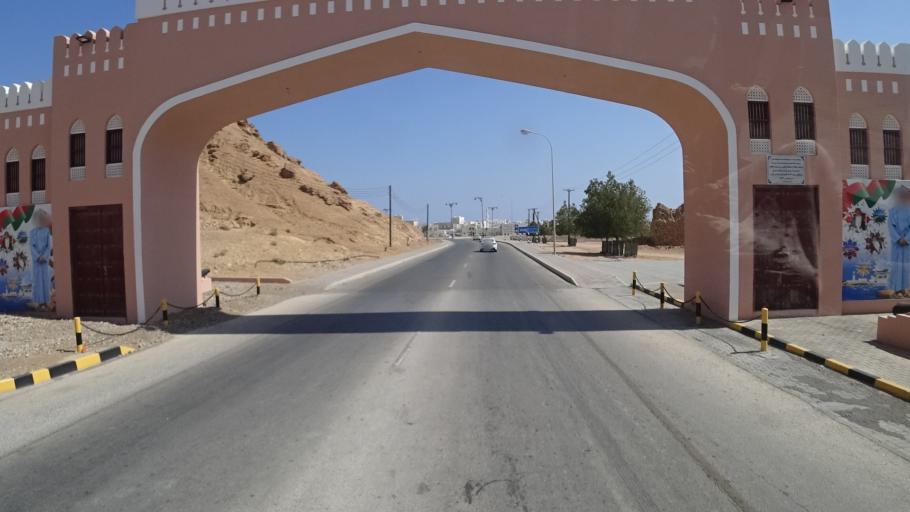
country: OM
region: Ash Sharqiyah
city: Sur
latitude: 22.5612
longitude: 59.5414
